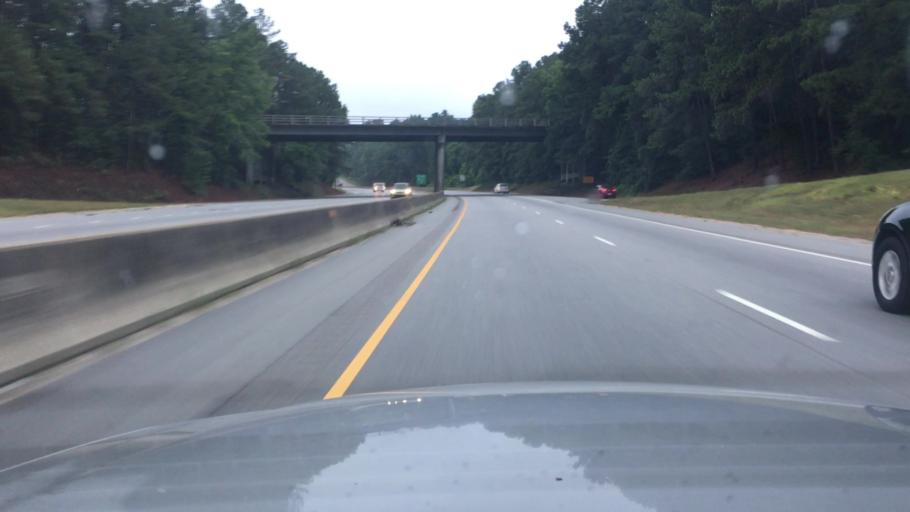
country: US
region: North Carolina
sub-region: Cumberland County
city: Fayetteville
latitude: 35.0619
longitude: -78.8911
